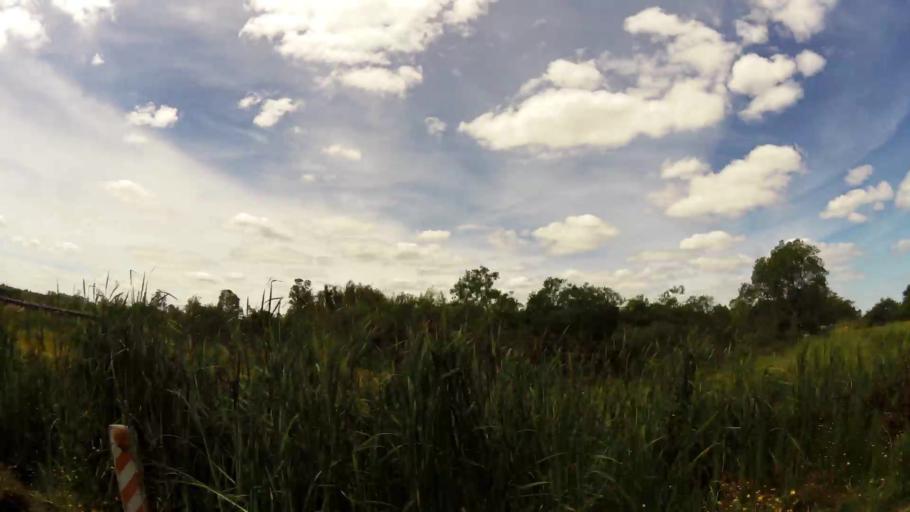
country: UY
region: Canelones
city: Empalme Olmos
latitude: -34.7881
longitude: -55.8905
